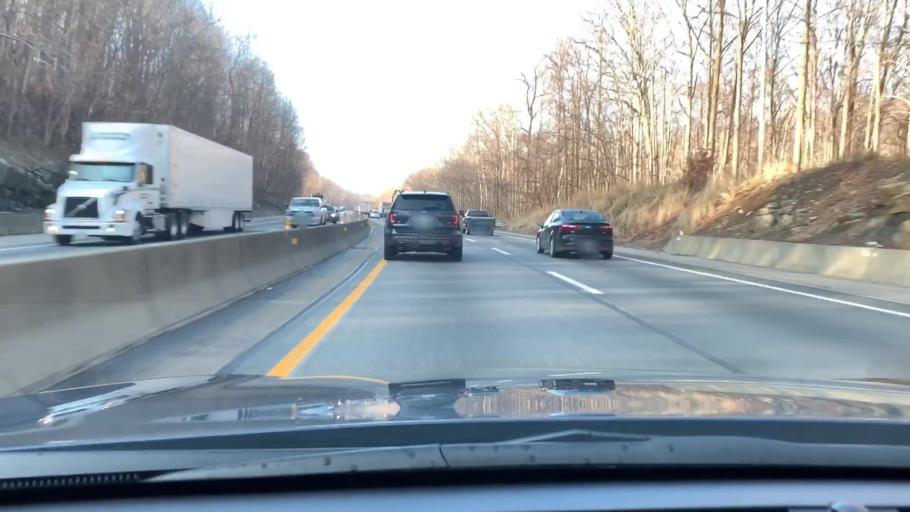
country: US
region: Pennsylvania
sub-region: Chester County
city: Downingtown
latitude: 40.0965
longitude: -75.7374
